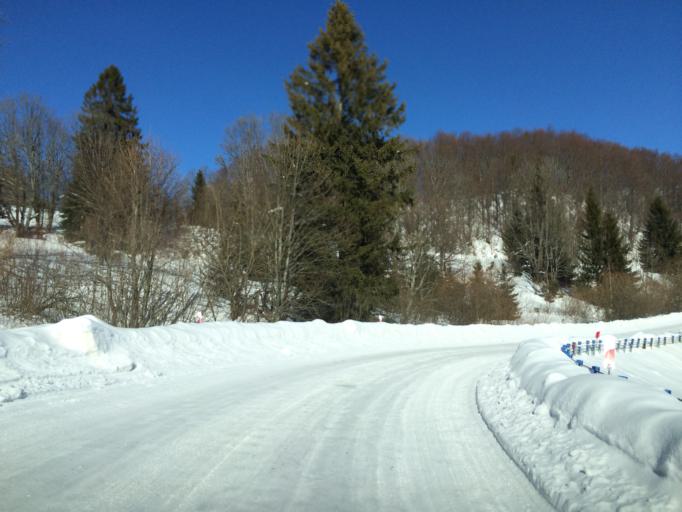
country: PL
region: Subcarpathian Voivodeship
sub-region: Powiat bieszczadzki
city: Lutowiska
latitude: 49.1413
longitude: 22.5507
